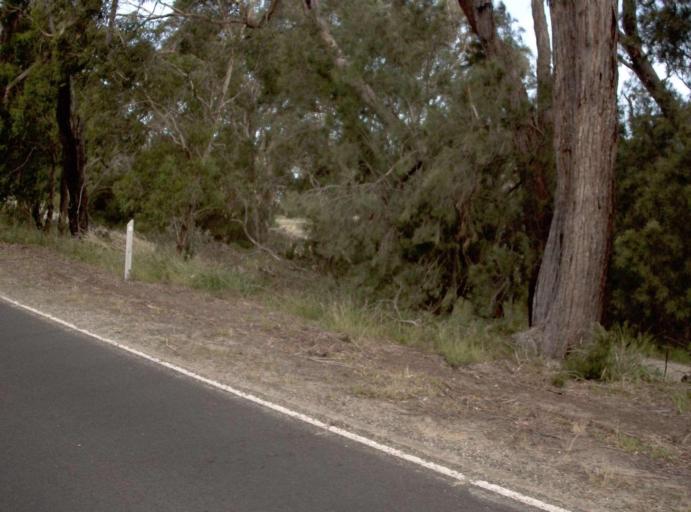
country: AU
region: Victoria
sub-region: Wellington
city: Sale
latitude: -38.2176
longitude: 147.1177
